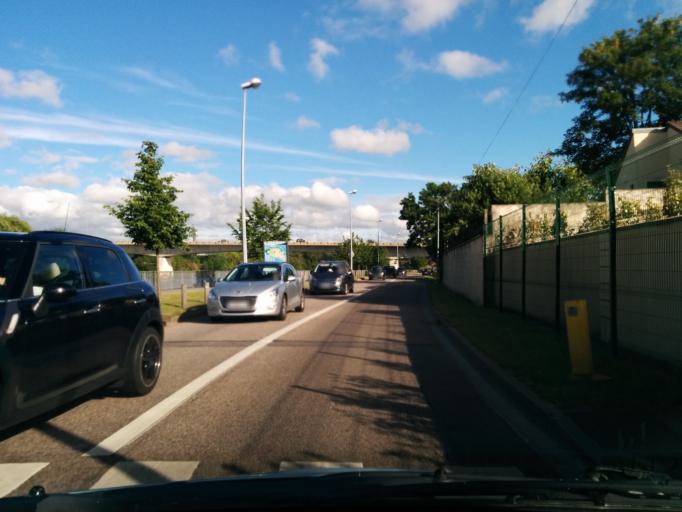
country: FR
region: Ile-de-France
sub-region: Departement des Yvelines
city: Mantes-la-Jolie
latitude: 48.9862
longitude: 1.7250
